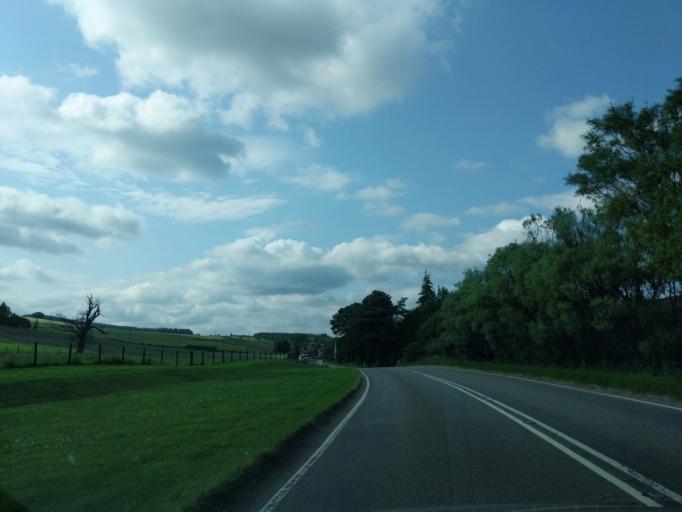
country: GB
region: Scotland
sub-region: Moray
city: Dufftown
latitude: 57.4590
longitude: -3.1320
